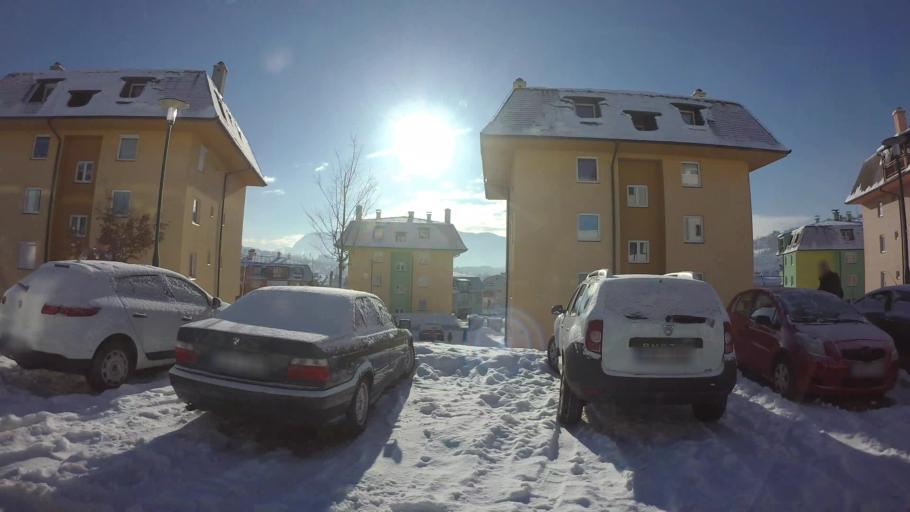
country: BA
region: Federation of Bosnia and Herzegovina
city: Kobilja Glava
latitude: 43.8815
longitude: 18.3986
